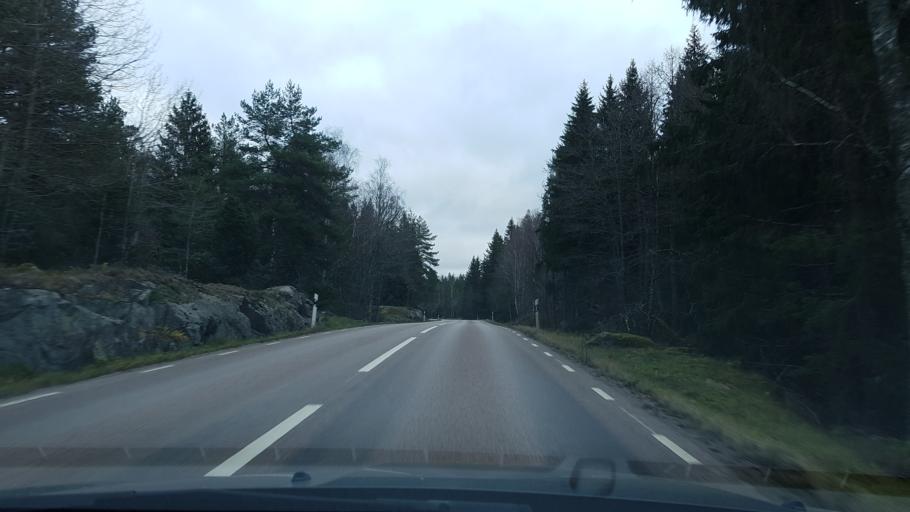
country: SE
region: Stockholm
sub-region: Norrtalje Kommun
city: Nykvarn
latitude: 59.9850
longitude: 18.2435
